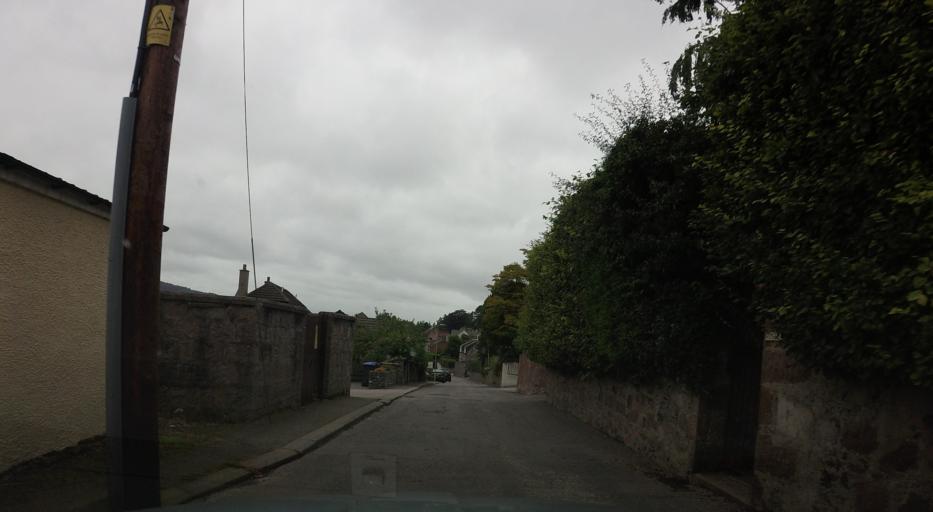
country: GB
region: Scotland
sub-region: Aberdeenshire
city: Banchory
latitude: 57.0518
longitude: -2.5020
